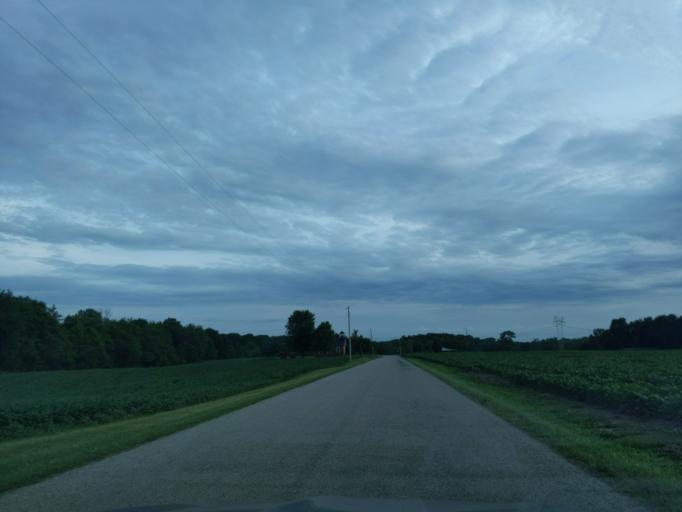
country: US
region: Indiana
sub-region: Ripley County
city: Sunman
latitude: 39.2946
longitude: -85.0904
